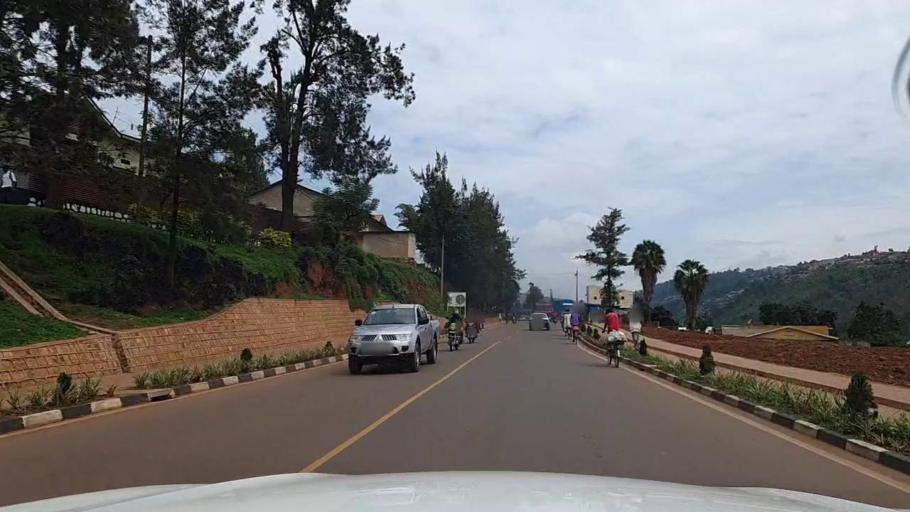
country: RW
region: Kigali
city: Kigali
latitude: -1.9331
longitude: 30.0454
